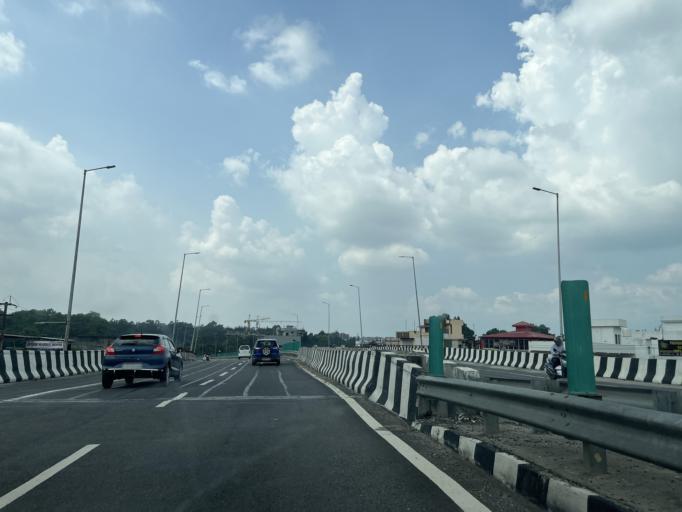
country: IN
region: Uttarakhand
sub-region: Dehradun
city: Raipur
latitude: 30.2626
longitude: 78.0863
